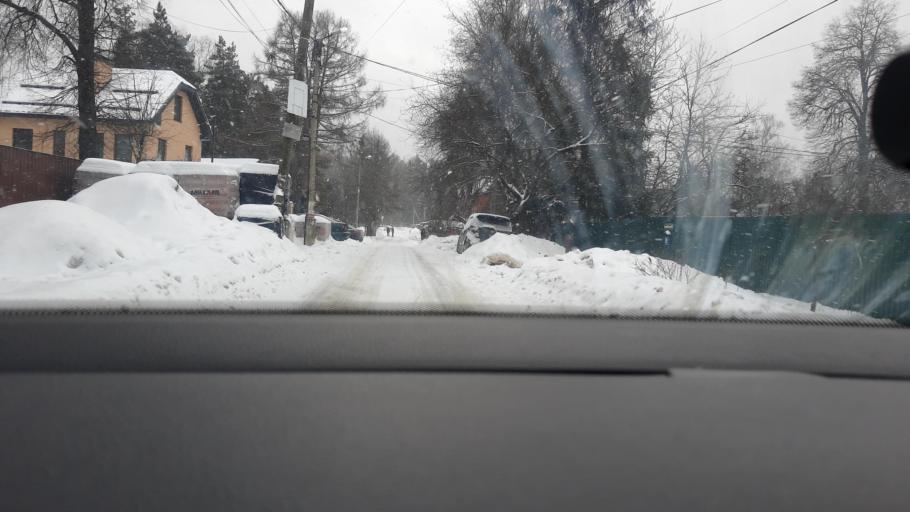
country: RU
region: Moskovskaya
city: Druzhba
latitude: 55.8829
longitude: 37.7406
